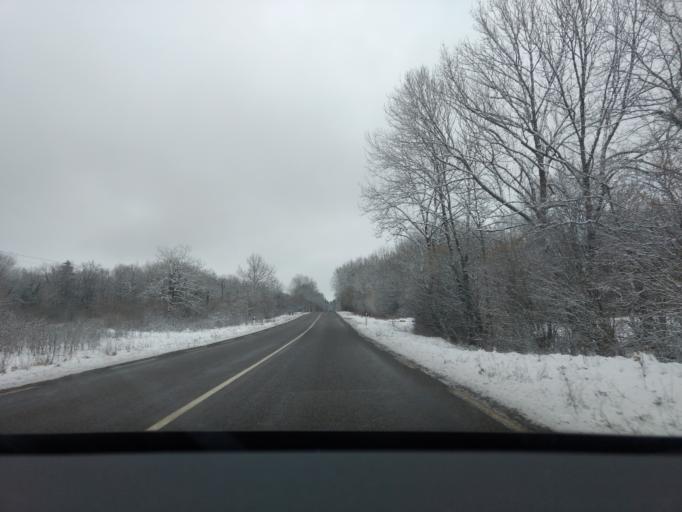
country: FR
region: Franche-Comte
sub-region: Departement du Jura
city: Champagnole
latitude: 46.7833
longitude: 5.8609
